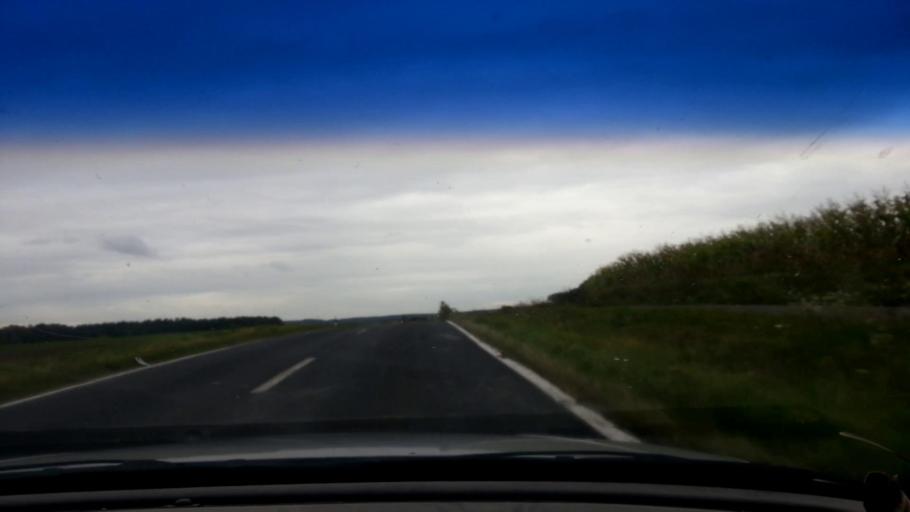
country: DE
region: Bavaria
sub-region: Upper Franconia
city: Priesendorf
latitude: 49.8875
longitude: 10.6516
